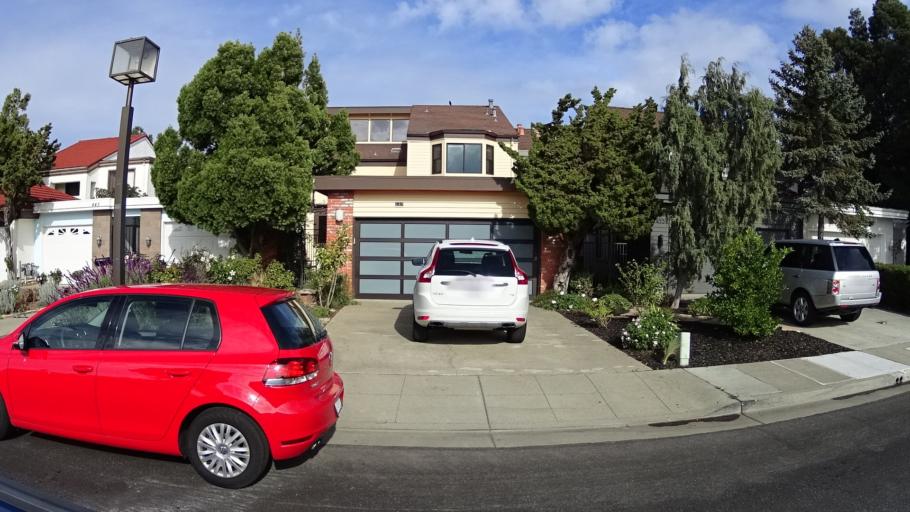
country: US
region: California
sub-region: San Mateo County
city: Redwood Shores
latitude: 37.5303
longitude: -122.2514
